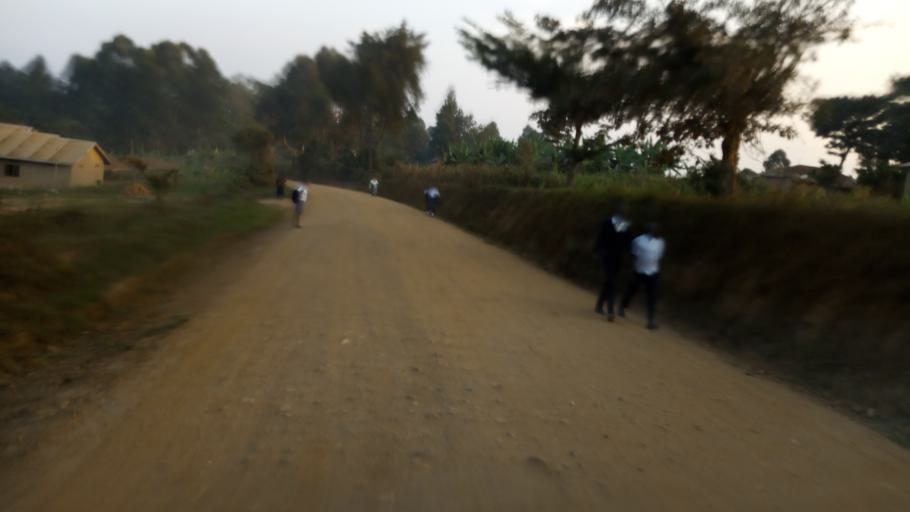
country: UG
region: Western Region
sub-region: Rukungiri District
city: Rukungiri
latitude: -0.7706
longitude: 29.9263
